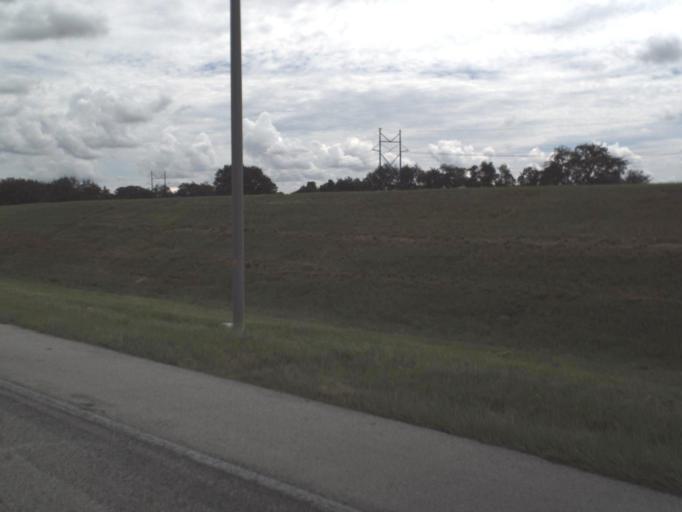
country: US
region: Florida
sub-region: Polk County
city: Polk City
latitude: 28.1725
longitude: -81.7656
